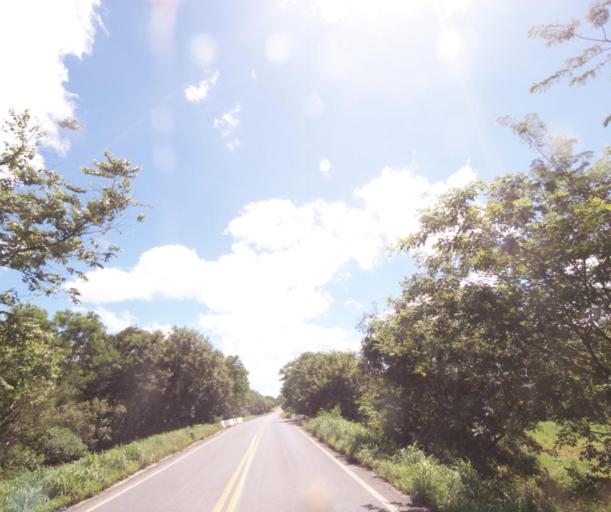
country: BR
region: Bahia
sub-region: Sao Felix Do Coribe
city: Santa Maria da Vitoria
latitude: -13.3974
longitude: -44.1395
